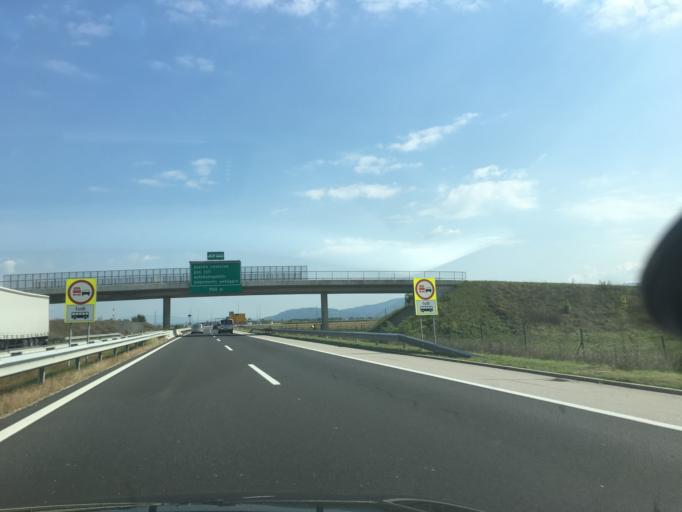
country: SI
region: Krsko
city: Leskovec pri Krskem
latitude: 45.9141
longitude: 15.4563
